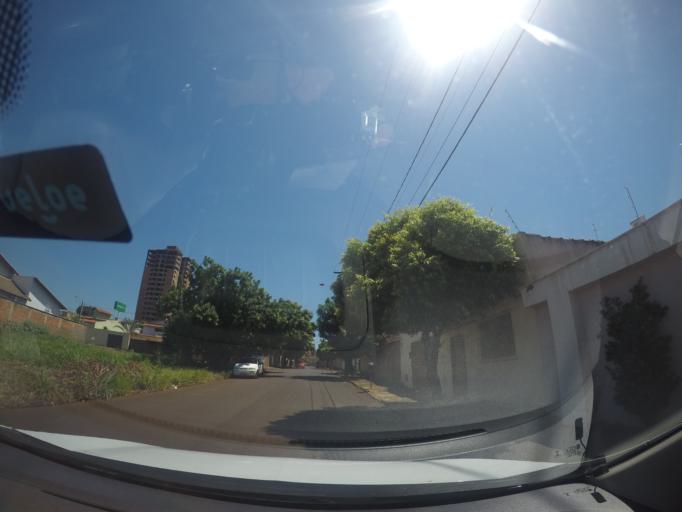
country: BR
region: Goias
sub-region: Itumbiara
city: Itumbiara
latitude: -18.4112
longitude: -49.2039
